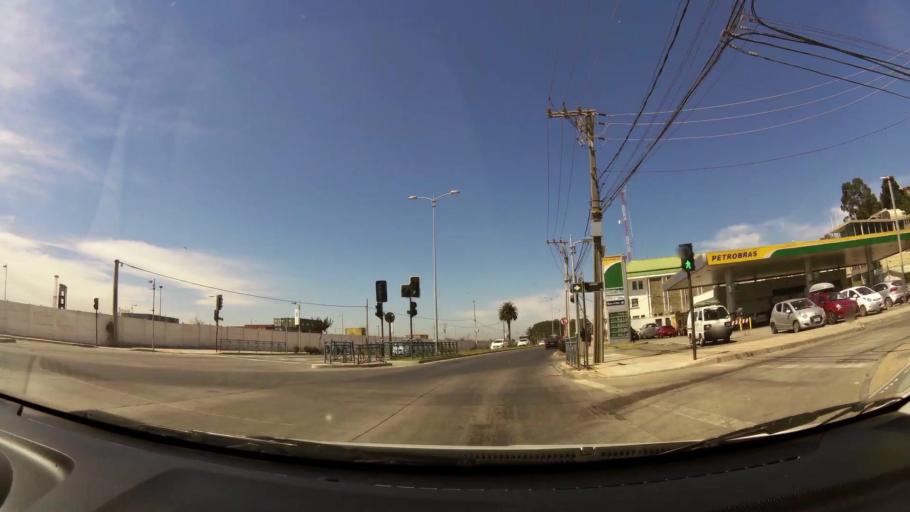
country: CL
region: Biobio
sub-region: Provincia de Concepcion
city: Talcahuano
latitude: -36.7153
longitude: -73.1096
